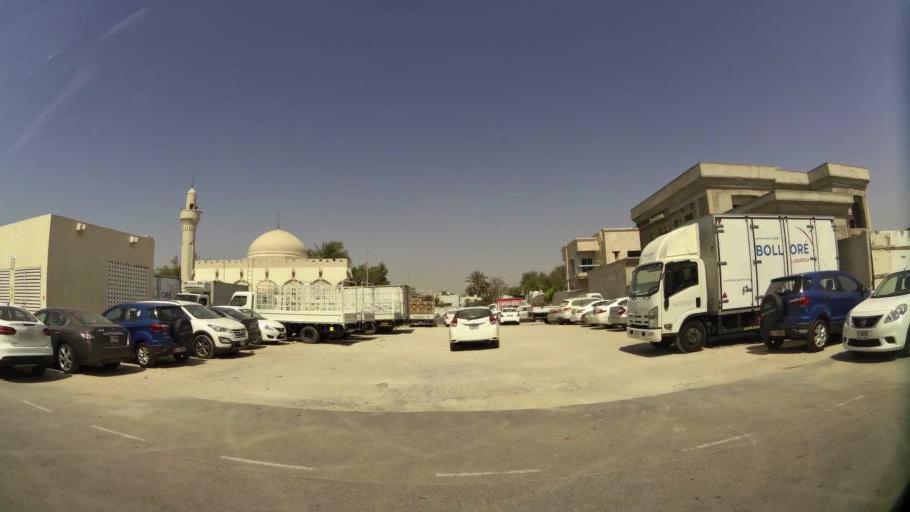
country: AE
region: Ash Shariqah
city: Sharjah
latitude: 25.2692
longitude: 55.3608
